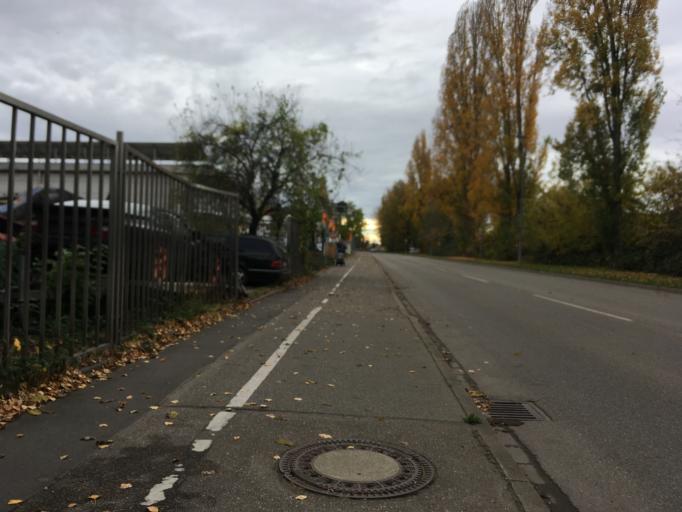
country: DE
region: Baden-Wuerttemberg
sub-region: Freiburg Region
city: Breisach am Rhein
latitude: 48.0402
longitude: 7.5725
